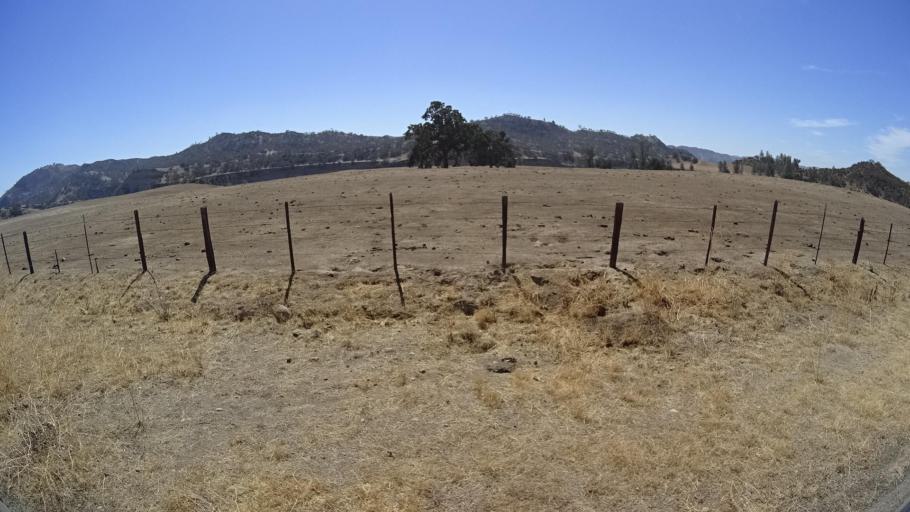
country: US
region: California
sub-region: Fresno County
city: Coalinga
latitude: 36.0998
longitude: -120.7001
